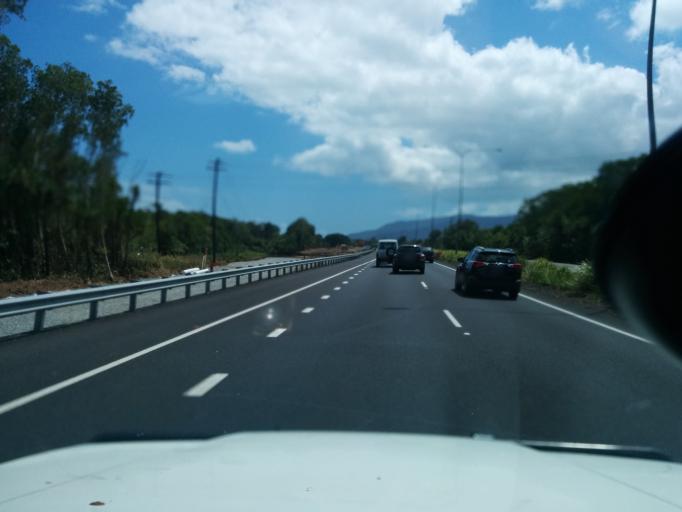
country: AU
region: Queensland
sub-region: Cairns
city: Woree
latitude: -16.9506
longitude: 145.7538
